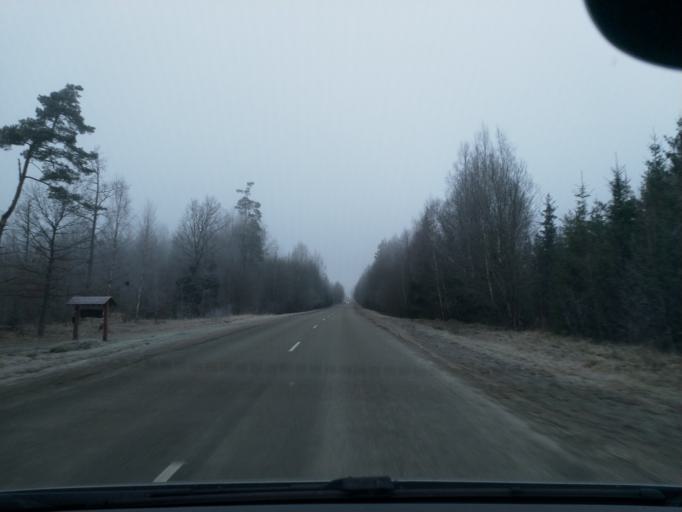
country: LV
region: Kuldigas Rajons
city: Kuldiga
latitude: 56.9124
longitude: 21.9331
